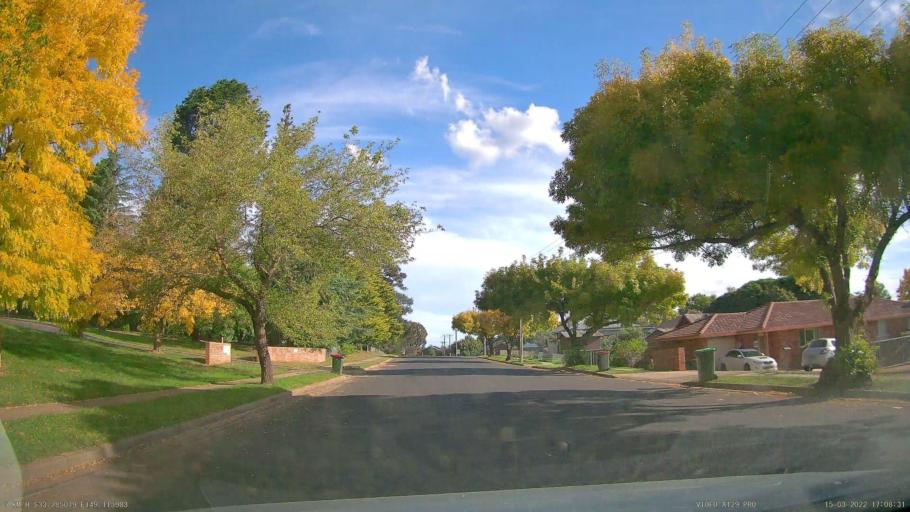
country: AU
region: New South Wales
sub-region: Orange Municipality
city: Orange
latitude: -33.2851
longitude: 149.1160
